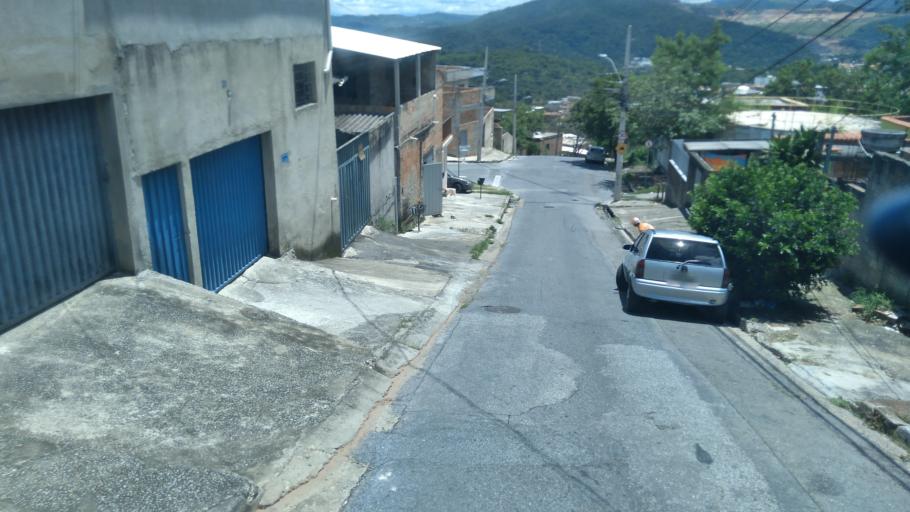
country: BR
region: Minas Gerais
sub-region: Belo Horizonte
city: Belo Horizonte
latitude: -19.8587
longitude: -43.8808
